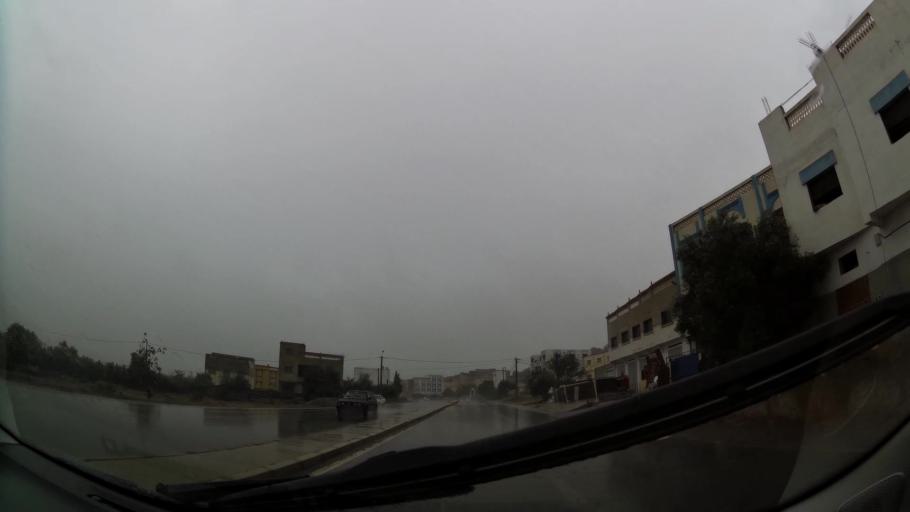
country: MA
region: Taza-Al Hoceima-Taounate
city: Imzourene
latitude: 35.1259
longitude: -3.8456
